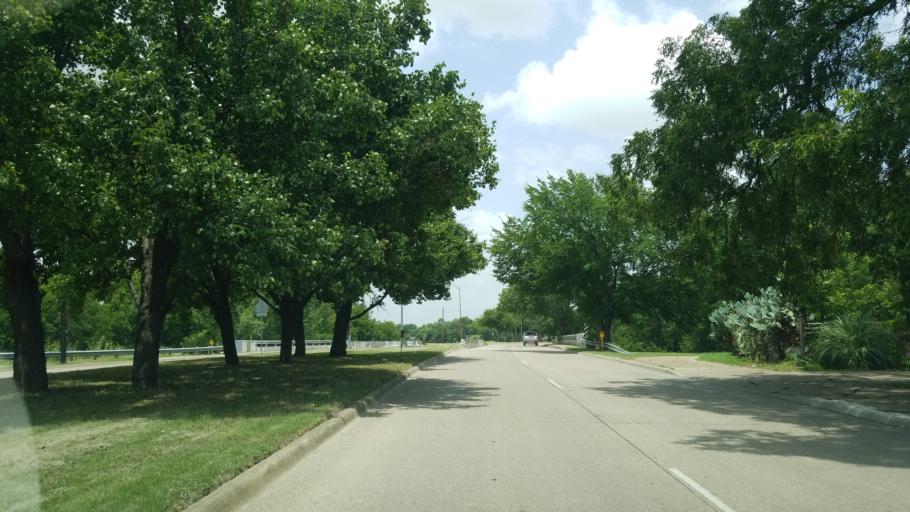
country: US
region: Texas
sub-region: Dallas County
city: Cockrell Hill
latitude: 32.7888
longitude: -96.8933
